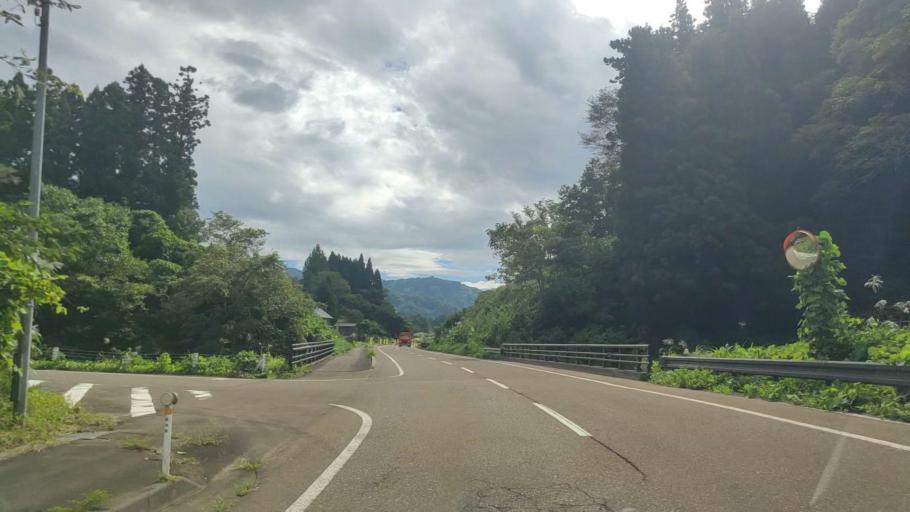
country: JP
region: Niigata
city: Arai
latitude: 36.9521
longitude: 138.2783
